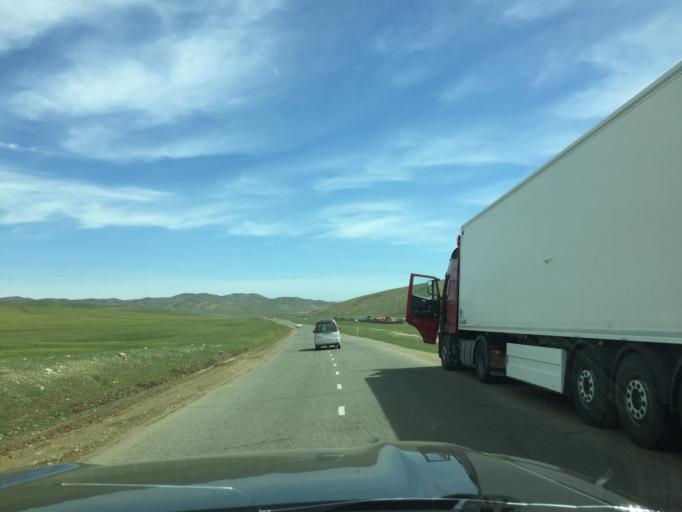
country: MN
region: Central Aimak
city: Bornuur
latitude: 48.6692
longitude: 106.1353
